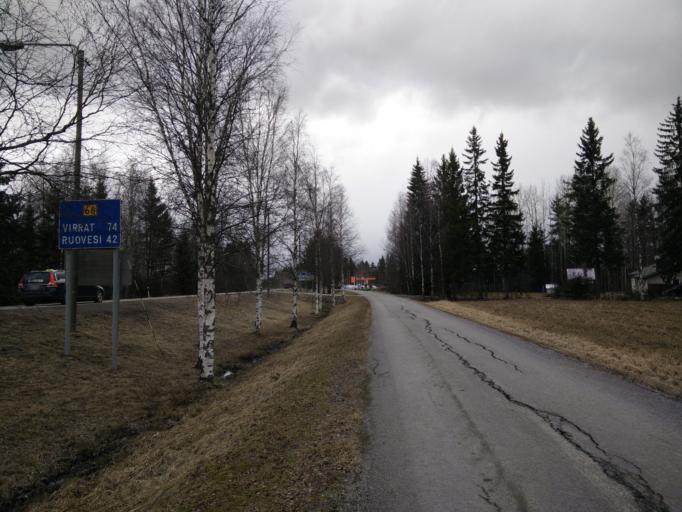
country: FI
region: Pirkanmaa
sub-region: Tampere
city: Orivesi
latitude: 61.6904
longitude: 24.3565
